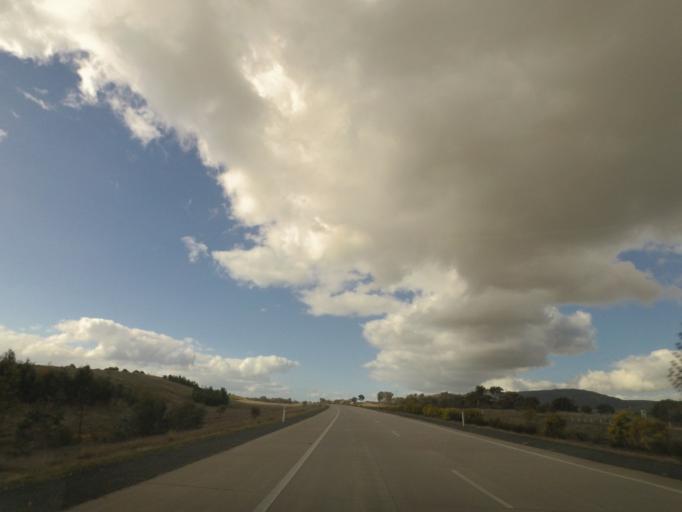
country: AU
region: New South Wales
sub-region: Greater Hume Shire
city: Holbrook
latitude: -35.7019
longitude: 147.3313
